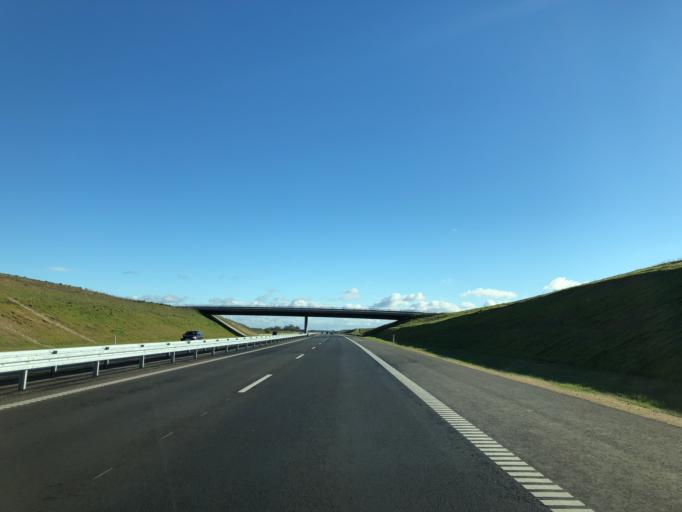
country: DK
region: Central Jutland
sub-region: Holstebro Kommune
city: Holstebro
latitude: 56.3812
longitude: 8.6740
